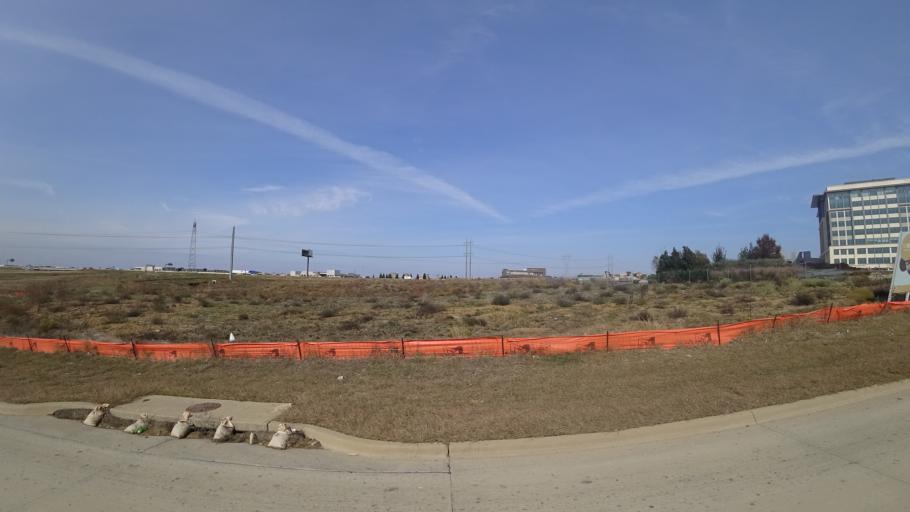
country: US
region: Texas
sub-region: Denton County
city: The Colony
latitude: 33.0591
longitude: -96.8955
